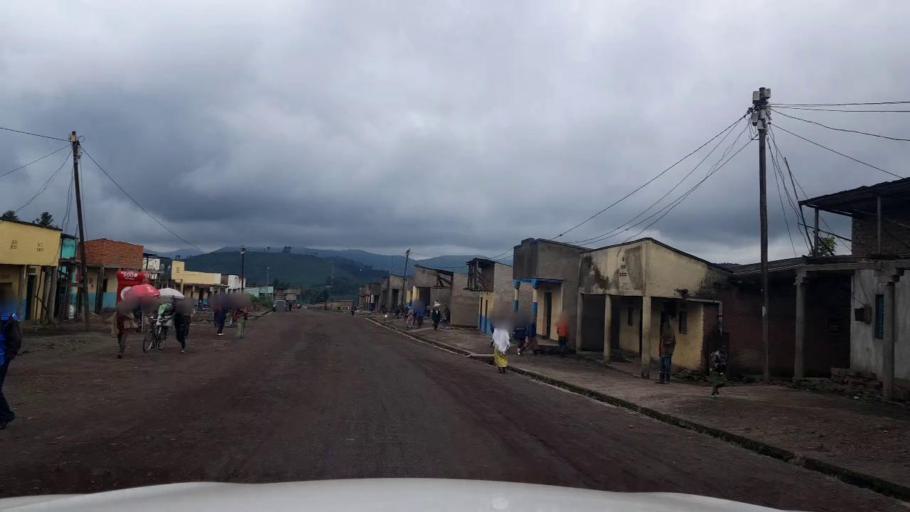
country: RW
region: Northern Province
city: Musanze
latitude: -1.6030
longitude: 29.4512
